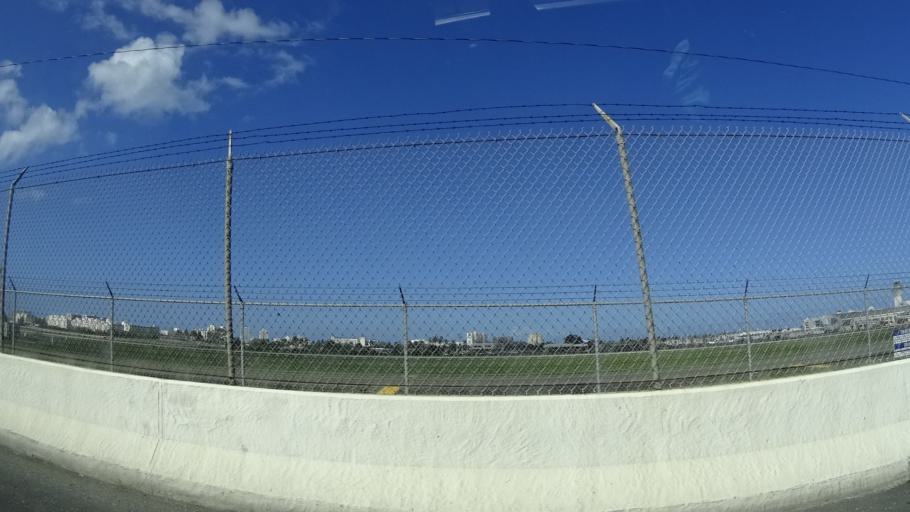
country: PR
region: Carolina
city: Carolina
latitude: 18.4320
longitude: -66.0098
